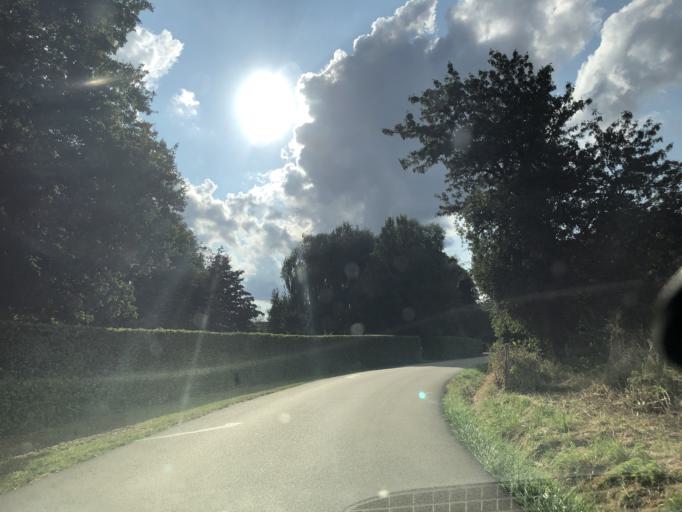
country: FR
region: Bourgogne
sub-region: Departement de l'Yonne
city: Charbuy
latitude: 47.8228
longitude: 3.4790
